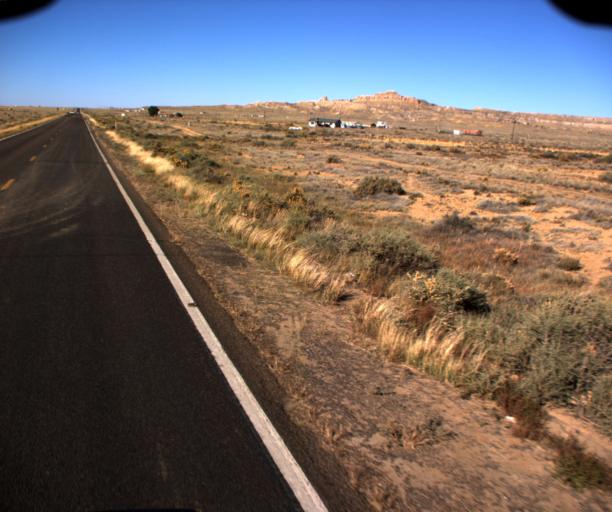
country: US
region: Arizona
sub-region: Navajo County
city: First Mesa
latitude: 35.7986
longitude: -110.4558
